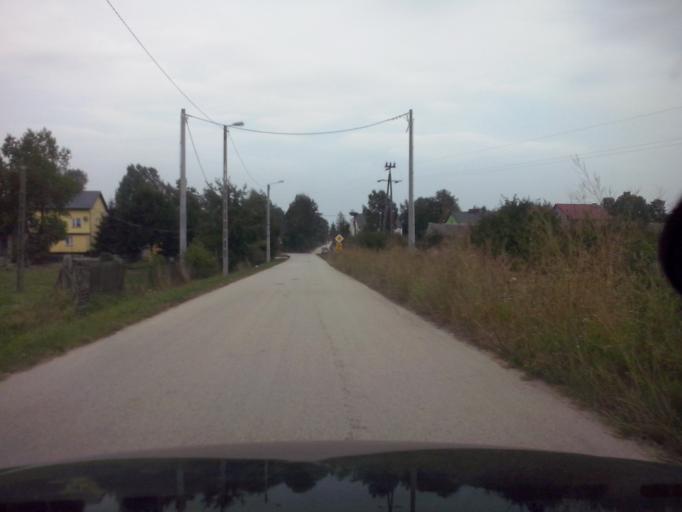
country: PL
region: Swietokrzyskie
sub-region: Powiat kielecki
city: Morawica
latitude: 50.6950
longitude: 20.5793
